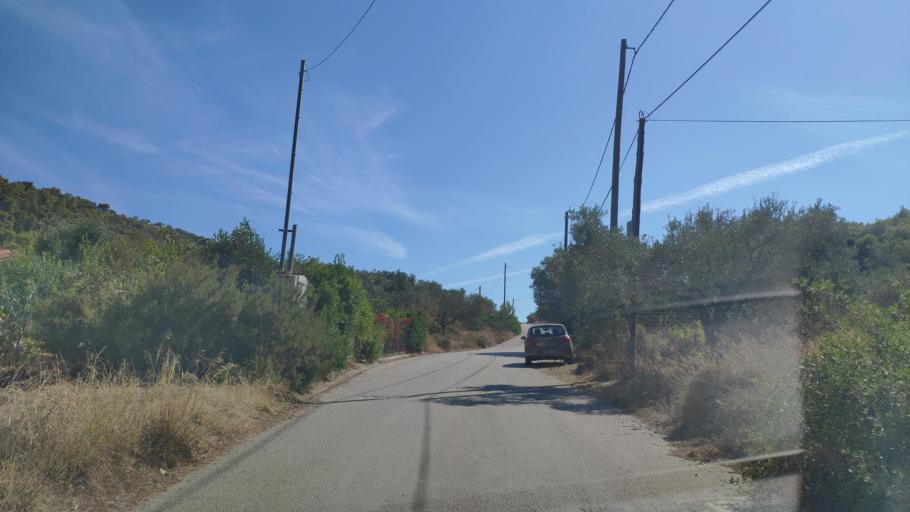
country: GR
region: Attica
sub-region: Nomarchia Anatolikis Attikis
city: Kouvaras
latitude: 37.8366
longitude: 23.9893
